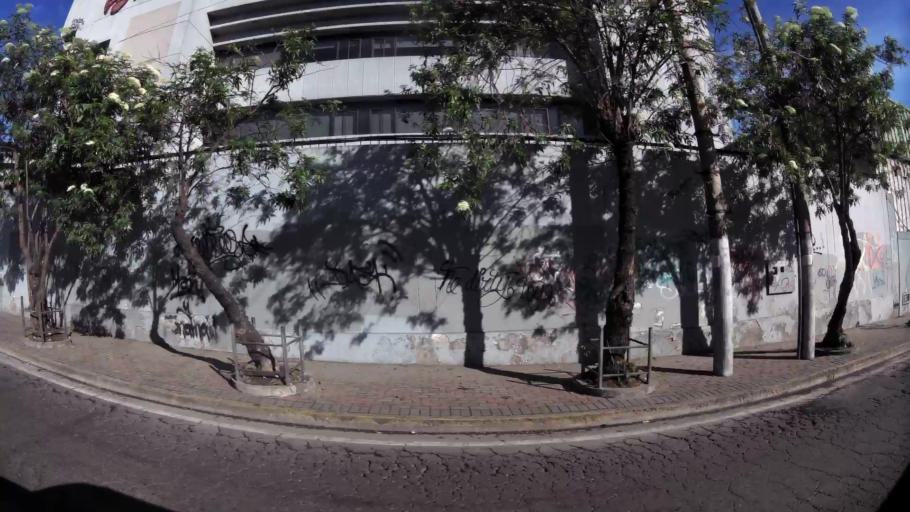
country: EC
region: Pichincha
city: Quito
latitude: -0.2930
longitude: -78.5398
